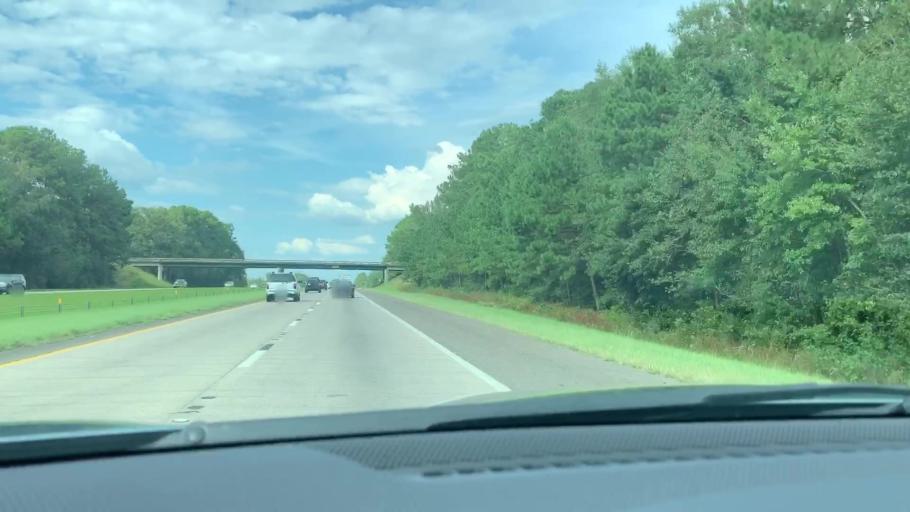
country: US
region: South Carolina
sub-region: Hampton County
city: Yemassee
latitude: 32.6770
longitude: -80.8823
